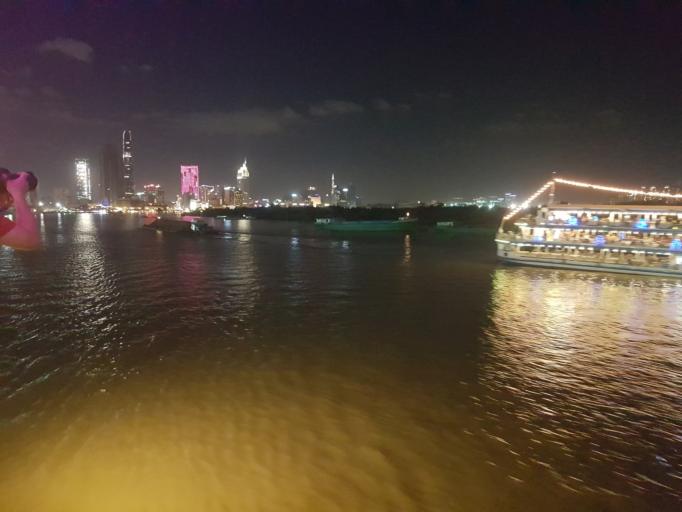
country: VN
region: Ho Chi Minh City
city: Quan Bon
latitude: 10.7603
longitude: 106.7172
